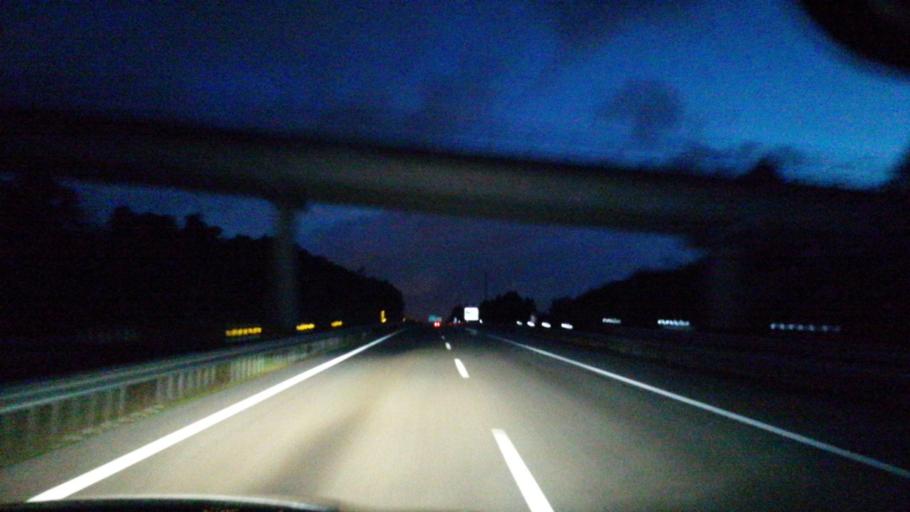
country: PT
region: Porto
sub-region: Lousada
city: Lousada
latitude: 41.3176
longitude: -8.2438
